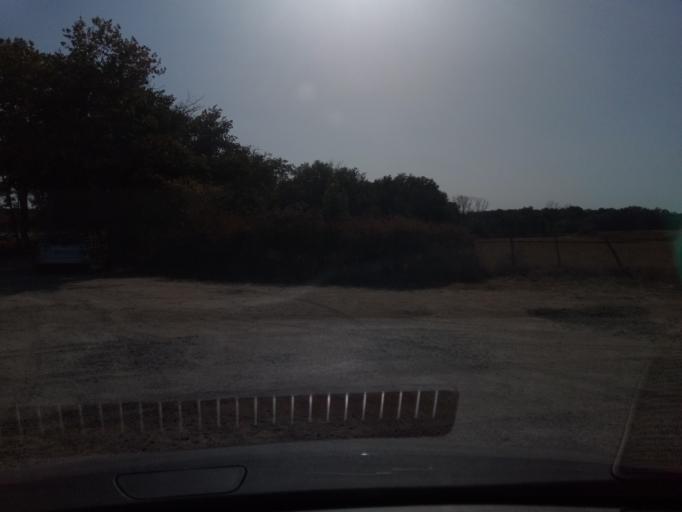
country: FR
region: Centre
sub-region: Departement de l'Indre
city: Le Blanc
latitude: 46.7113
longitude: 1.1538
